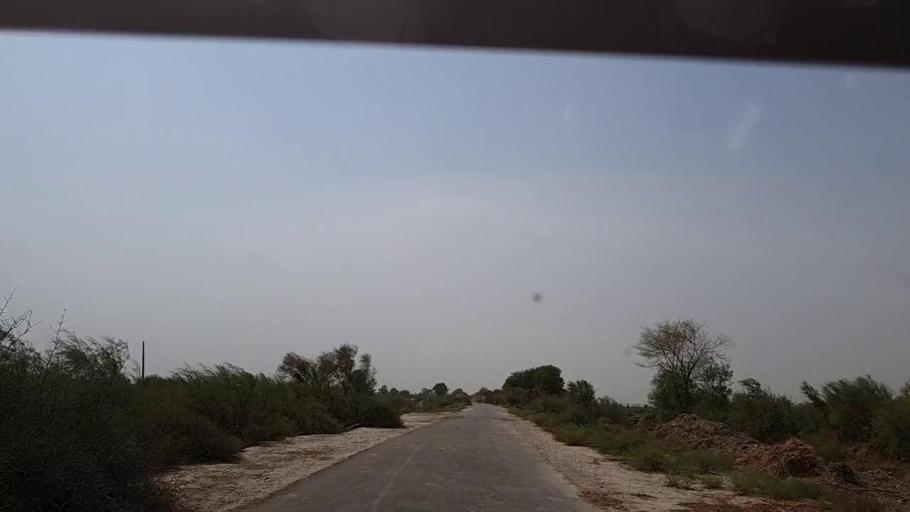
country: PK
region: Sindh
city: Khairpur Nathan Shah
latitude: 27.0335
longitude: 67.6793
